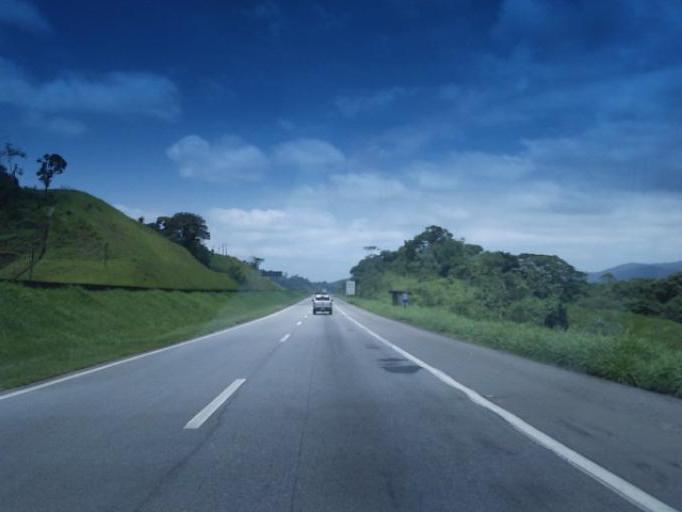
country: BR
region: Sao Paulo
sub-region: Miracatu
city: Miracatu
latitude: -24.1718
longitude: -47.3411
